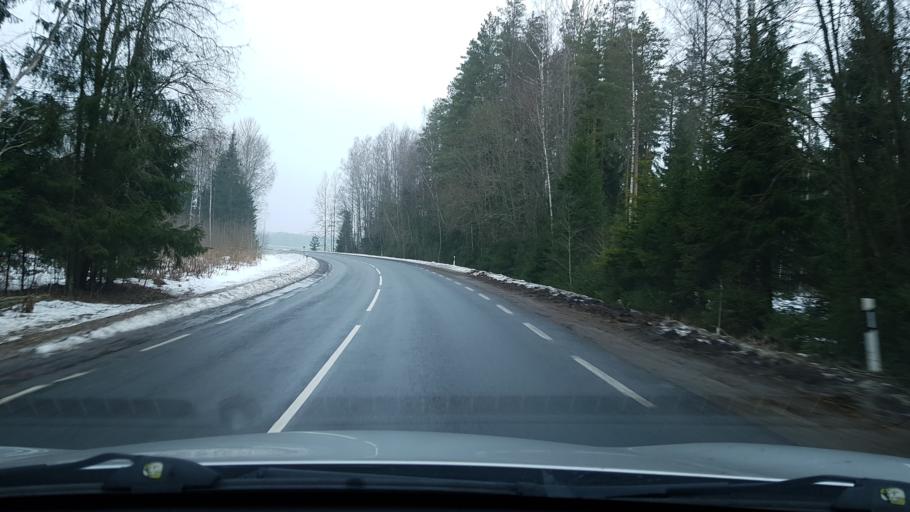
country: EE
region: Valgamaa
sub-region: Torva linn
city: Torva
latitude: 58.2057
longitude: 25.9500
